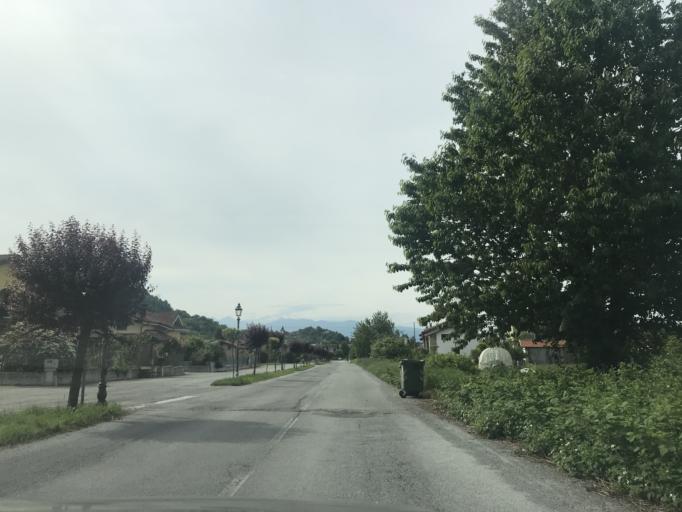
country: IT
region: Piedmont
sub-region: Provincia di Cuneo
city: Boves
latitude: 44.3211
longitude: 7.5578
